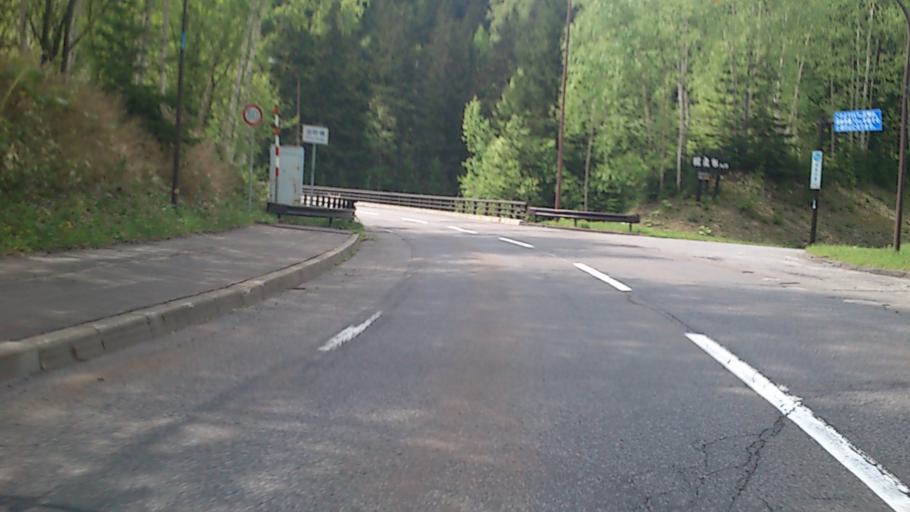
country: JP
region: Hokkaido
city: Kamikawa
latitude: 43.6628
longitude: 143.0348
